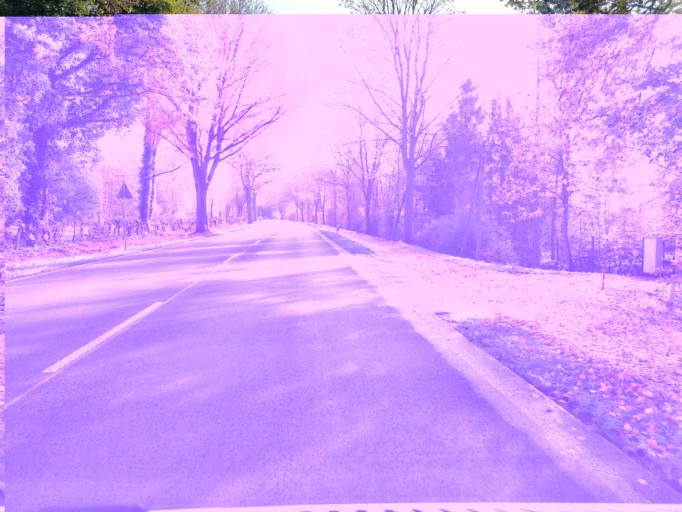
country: DE
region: North Rhine-Westphalia
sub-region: Regierungsbezirk Dusseldorf
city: Mehrhoog
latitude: 51.7617
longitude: 6.4718
